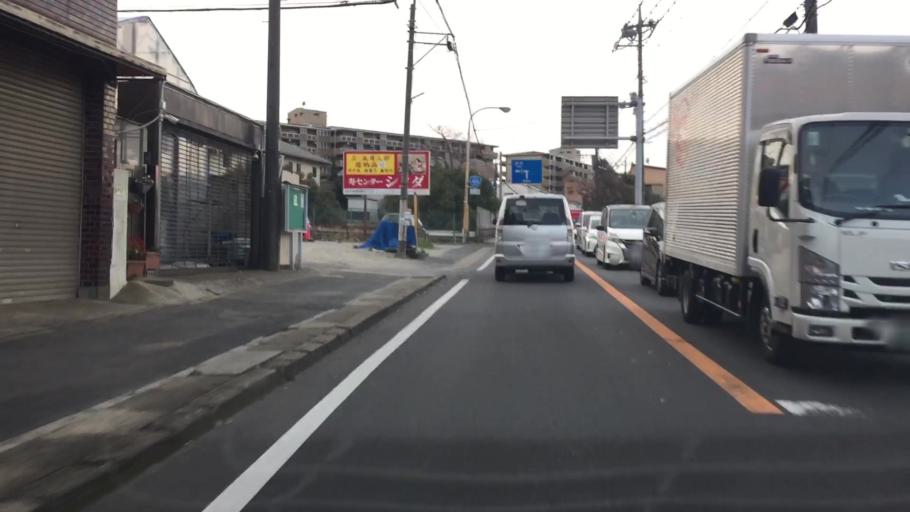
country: JP
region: Chiba
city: Matsudo
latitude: 35.7745
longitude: 139.9064
